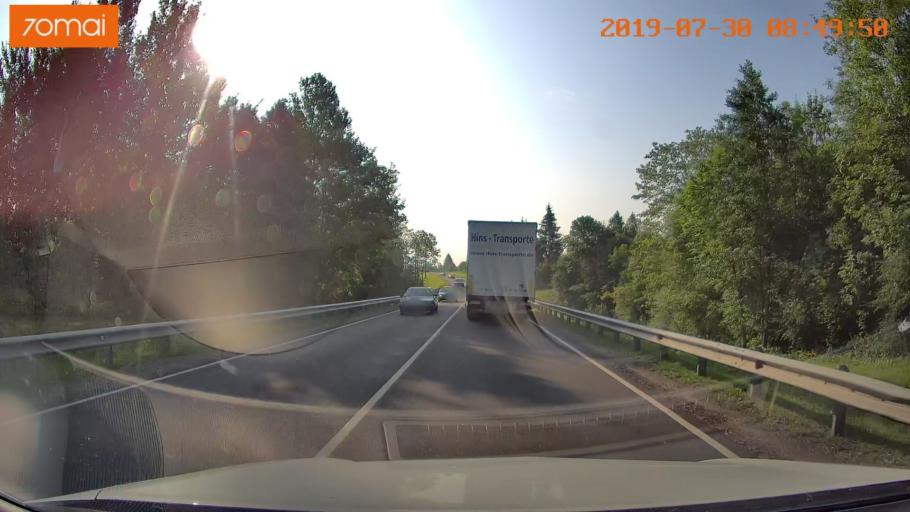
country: RU
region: Kaliningrad
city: Chernyakhovsk
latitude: 54.6108
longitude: 21.9291
